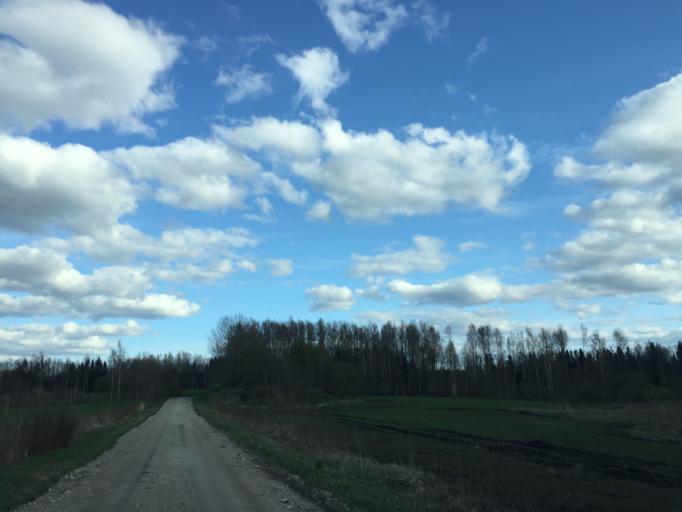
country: LV
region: Karsava
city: Karsava
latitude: 56.6764
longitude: 27.5275
